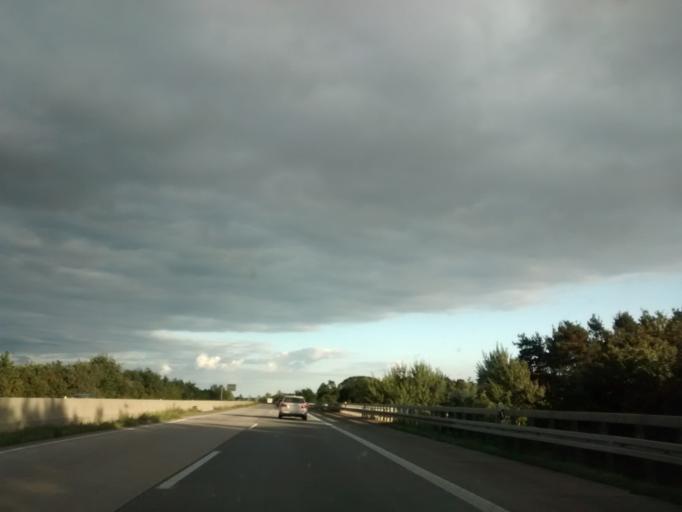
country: DE
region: North Rhine-Westphalia
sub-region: Regierungsbezirk Munster
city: Rheine
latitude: 52.3175
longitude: 7.4451
